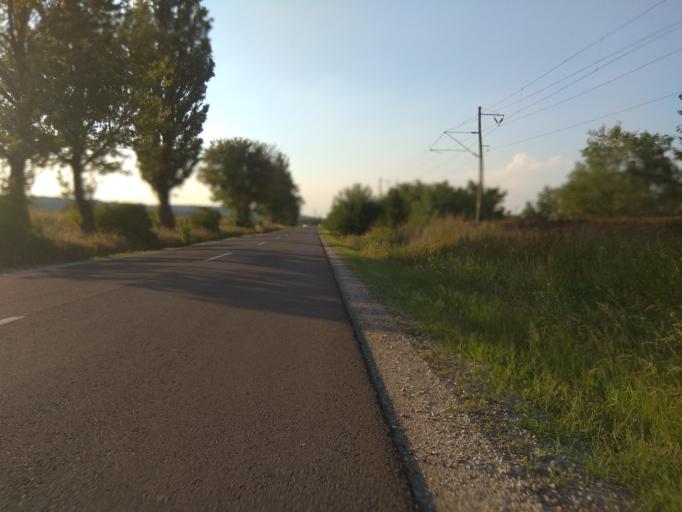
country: HU
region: Borsod-Abauj-Zemplen
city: Nyekladhaza
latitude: 47.9821
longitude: 20.8429
